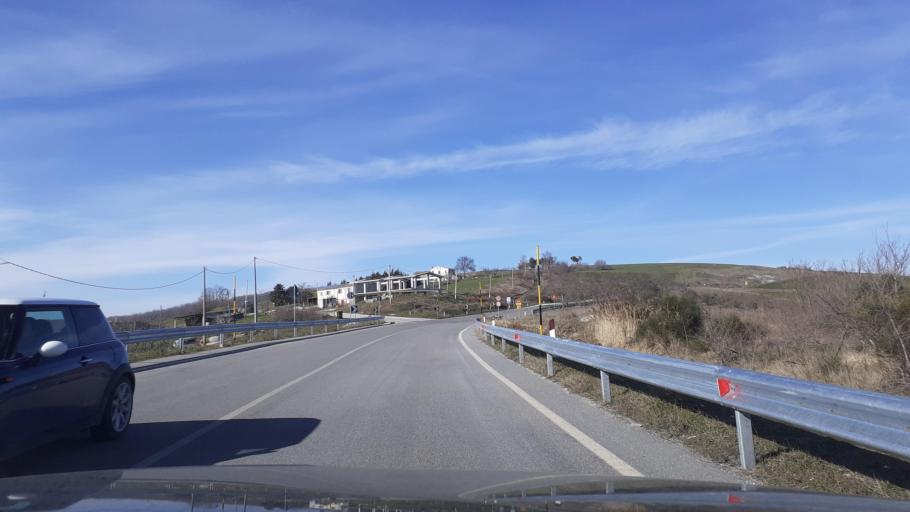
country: IT
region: Molise
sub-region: Provincia di Campobasso
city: Pietracupa
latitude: 41.6862
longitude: 14.5118
